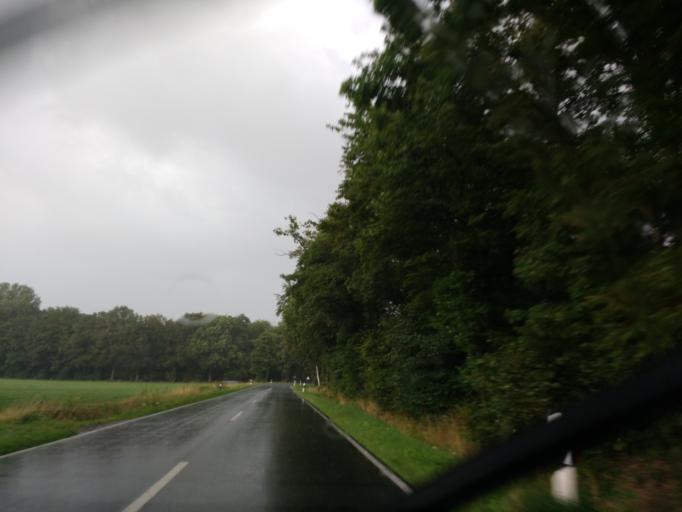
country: DE
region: North Rhine-Westphalia
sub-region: Regierungsbezirk Munster
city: Lienen
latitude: 52.1139
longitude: 7.9236
